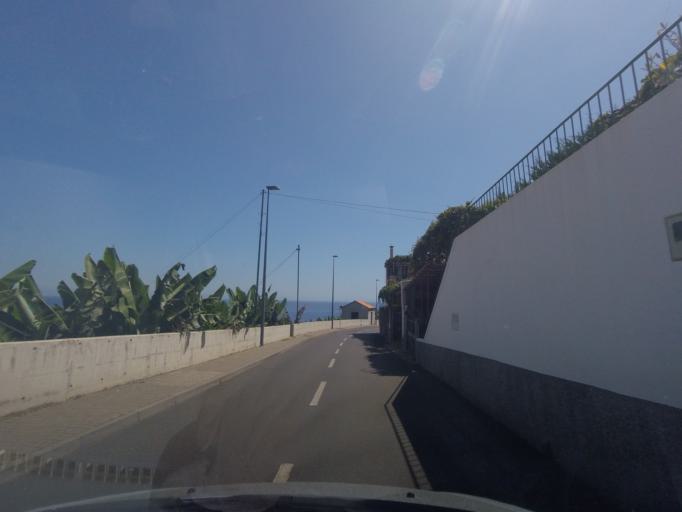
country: PT
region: Madeira
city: Camara de Lobos
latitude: 32.6465
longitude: -16.9623
